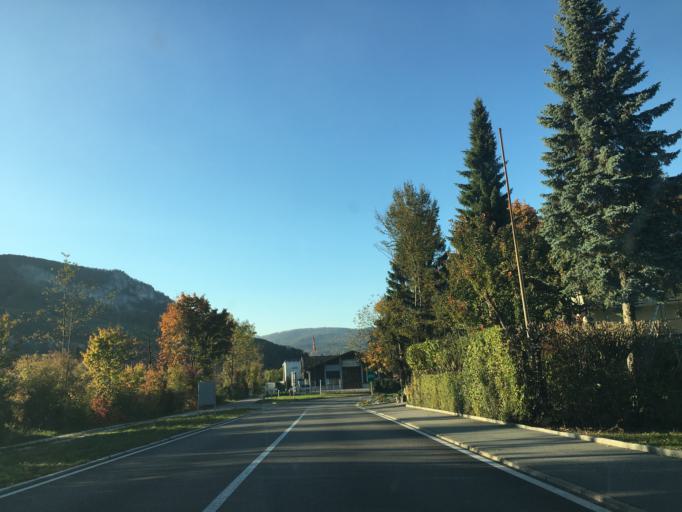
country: CH
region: Solothurn
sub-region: Bezirk Gaeu
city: Oensingen
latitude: 47.2890
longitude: 7.7133
